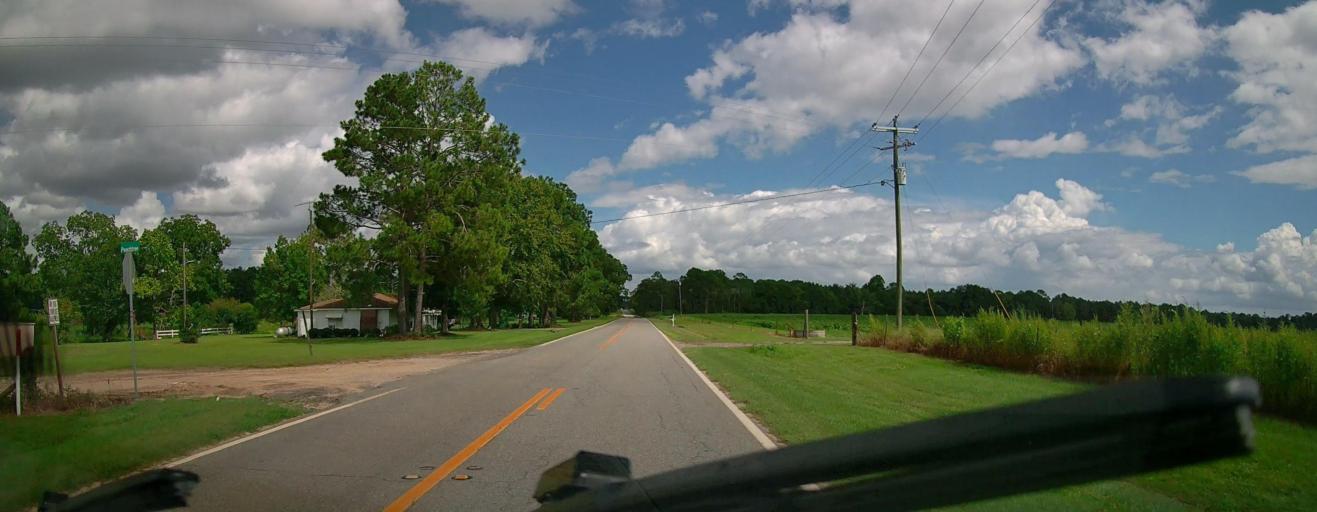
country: US
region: Georgia
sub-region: Ben Hill County
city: Fitzgerald
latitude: 31.6836
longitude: -83.2062
